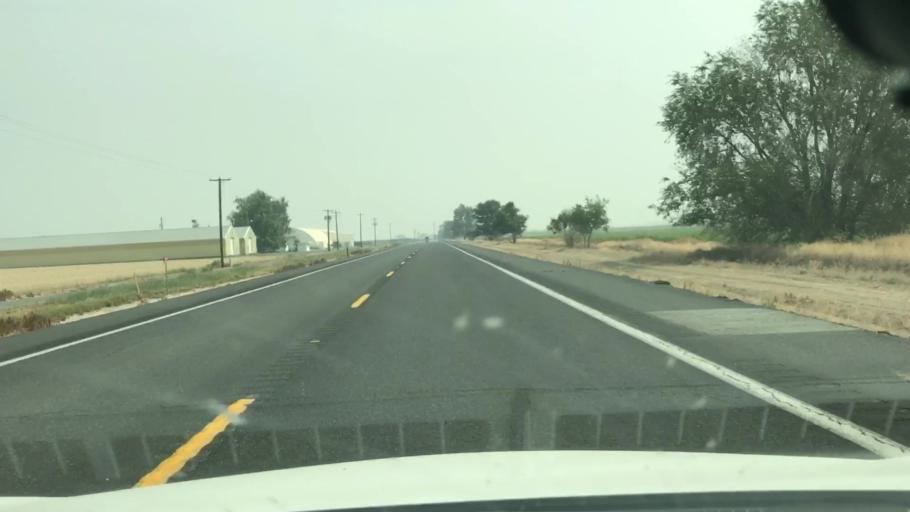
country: US
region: Washington
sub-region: Grant County
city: Quincy
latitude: 47.2343
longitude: -119.7551
